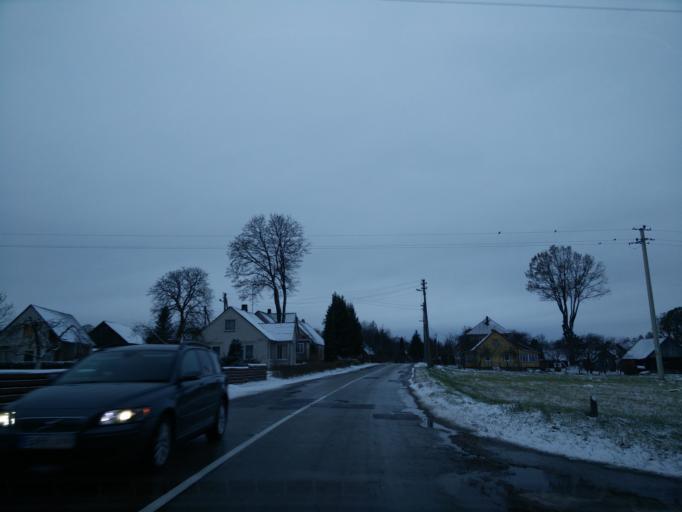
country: LT
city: Tytuveneliai
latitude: 55.5272
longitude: 23.2321
